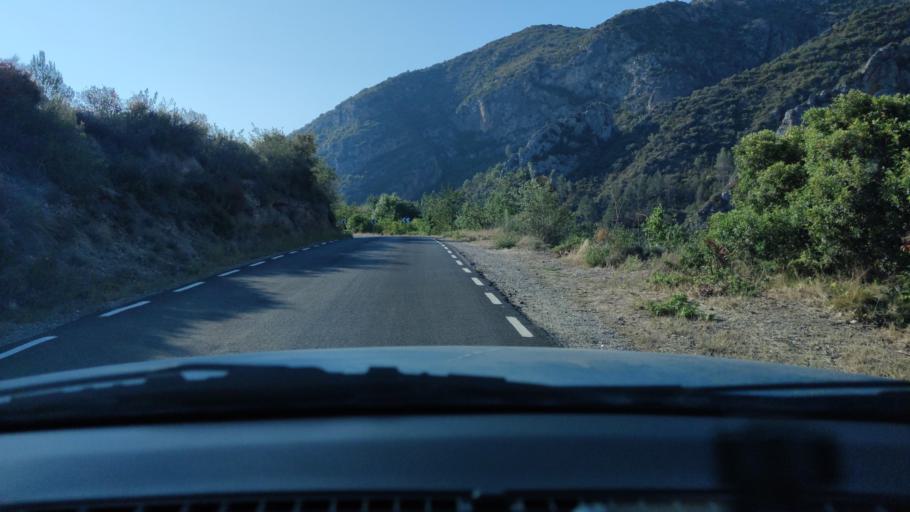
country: ES
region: Catalonia
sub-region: Provincia de Lleida
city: Camarasa
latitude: 41.8738
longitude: 0.8506
